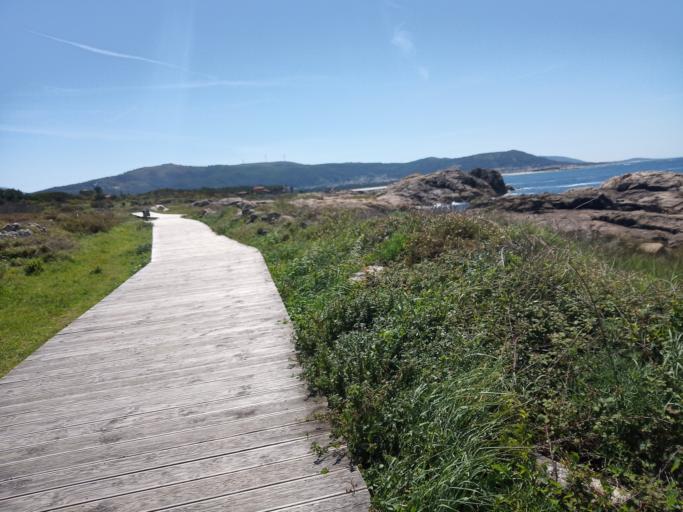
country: ES
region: Galicia
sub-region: Provincia de Pontevedra
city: A Guarda
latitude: 41.8782
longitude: -8.8792
